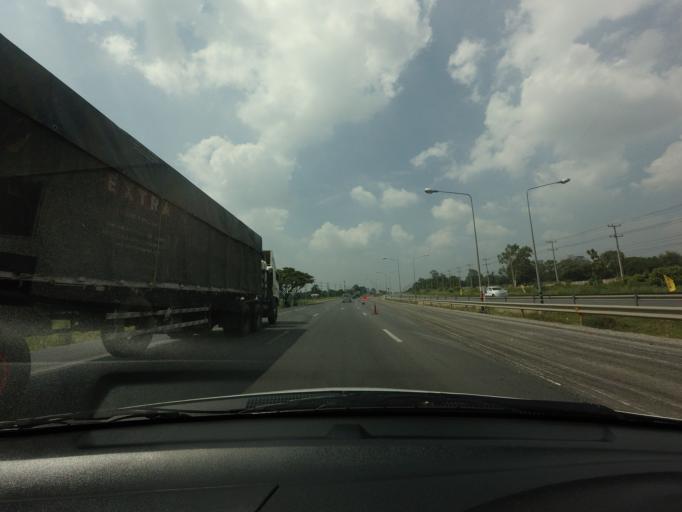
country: TH
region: Nakhon Ratchasima
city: Pak Chong
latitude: 14.6696
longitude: 101.4499
